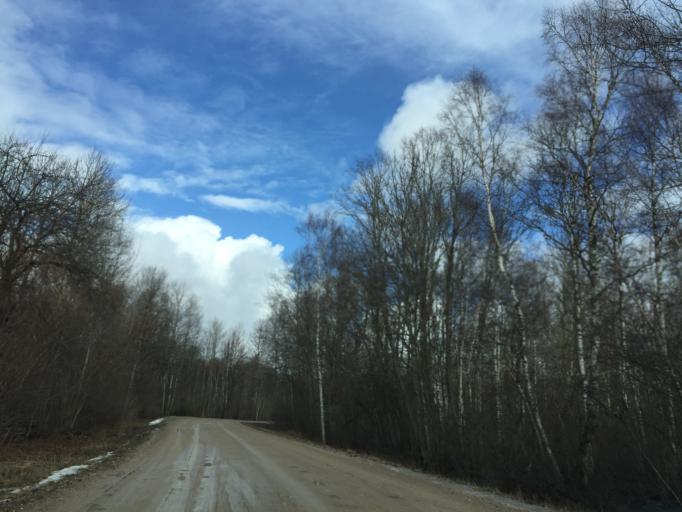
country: EE
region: Laeaene
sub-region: Lihula vald
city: Lihula
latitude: 58.7198
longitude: 23.8277
